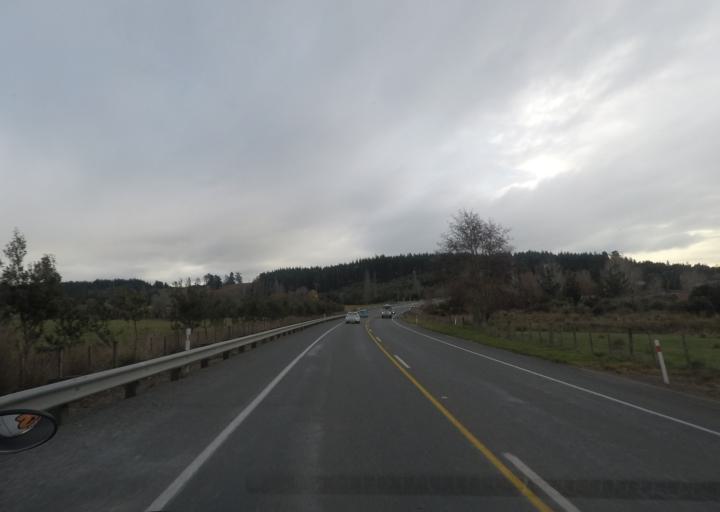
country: NZ
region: Tasman
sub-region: Tasman District
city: Mapua
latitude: -41.2806
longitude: 173.0709
